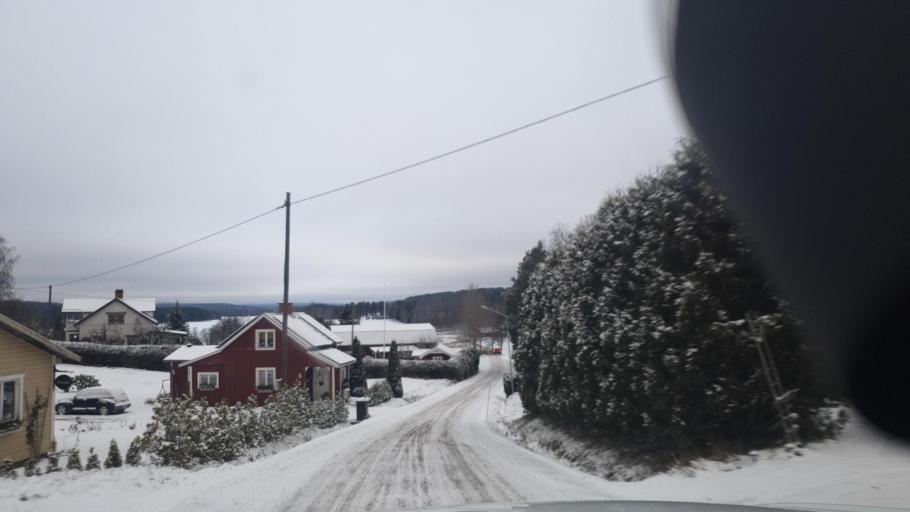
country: SE
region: Vaermland
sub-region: Karlstads Kommun
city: Edsvalla
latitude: 59.6068
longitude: 13.0666
